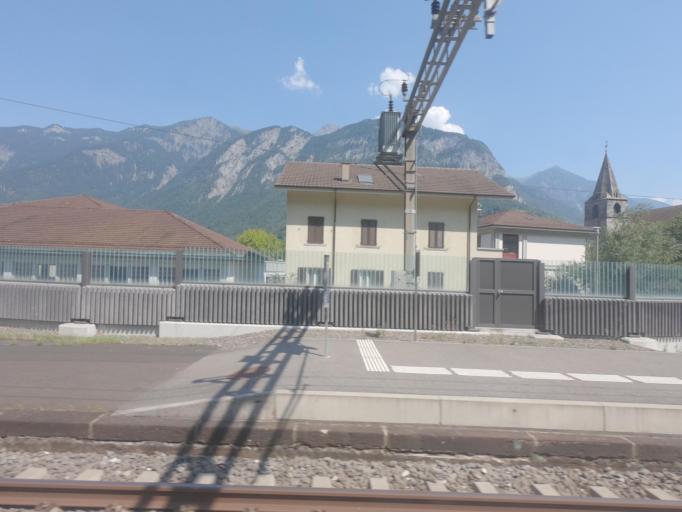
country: CH
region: Valais
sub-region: Saint-Maurice District
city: Saint-Maurice
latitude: 46.2183
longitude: 7.0023
